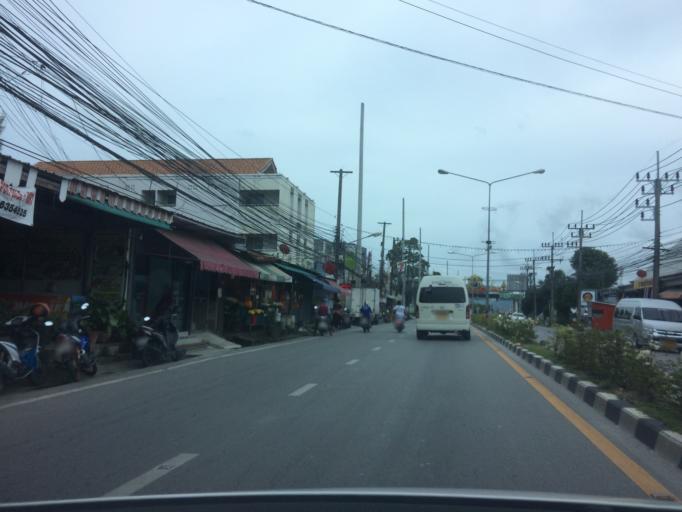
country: TH
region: Phuket
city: Mueang Phuket
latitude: 7.8621
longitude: 98.3696
